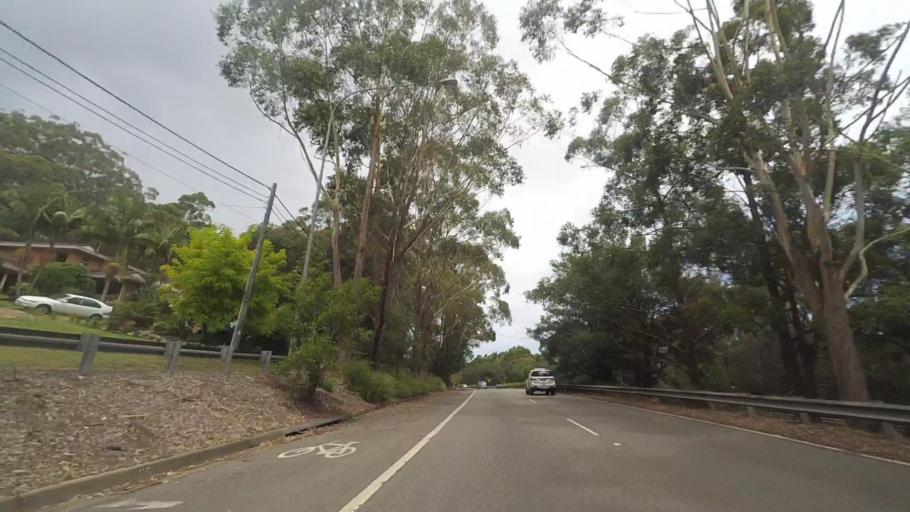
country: AU
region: New South Wales
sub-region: Wyong Shire
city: Berkeley Vale
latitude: -33.3490
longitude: 151.4316
